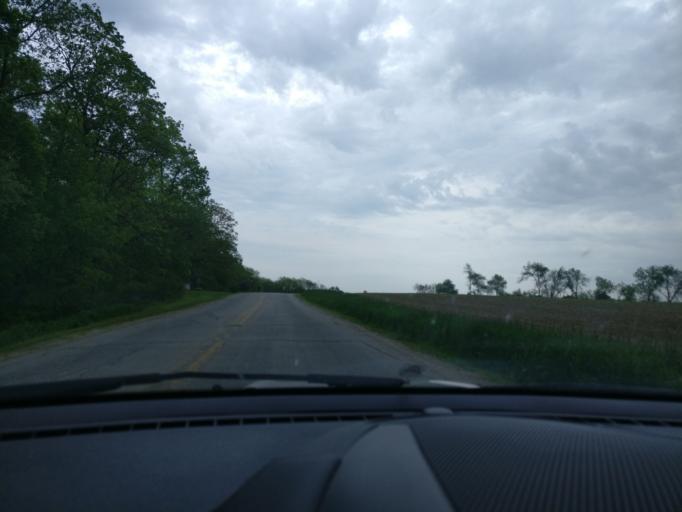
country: US
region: Wisconsin
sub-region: Lafayette County
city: Darlington
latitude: 42.7489
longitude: -89.9851
